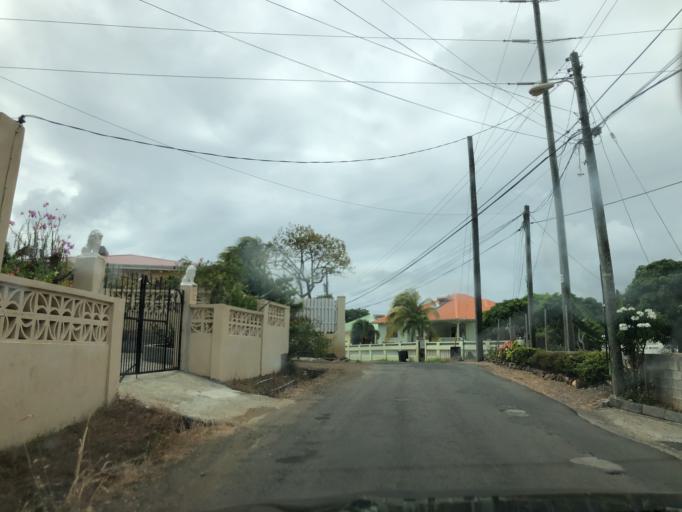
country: LC
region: Gros-Islet
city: Gros Islet
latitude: 14.0674
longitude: -60.9462
